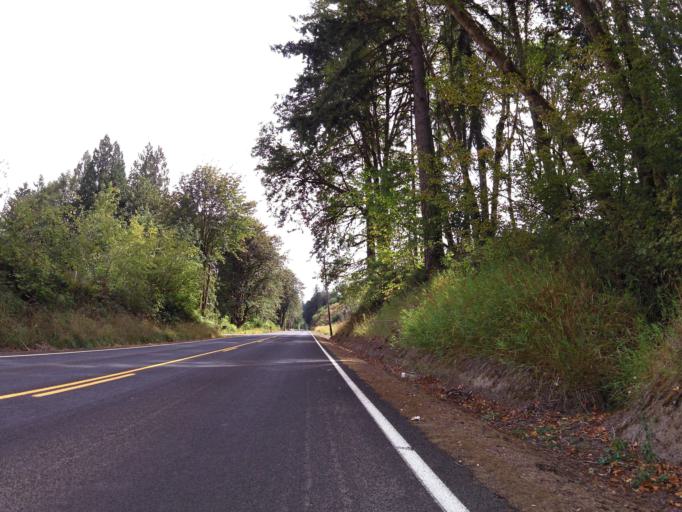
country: US
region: Washington
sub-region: Cowlitz County
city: Castle Rock
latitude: 46.3444
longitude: -122.9394
